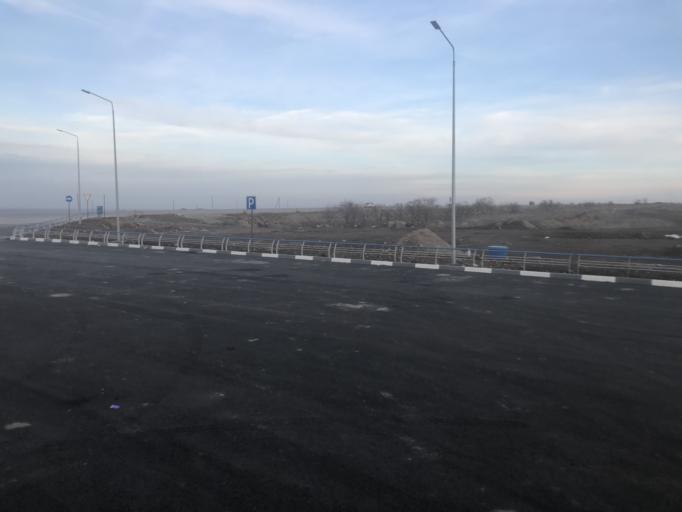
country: KG
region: Chuy
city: Ivanovka
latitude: 43.3986
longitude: 75.1168
